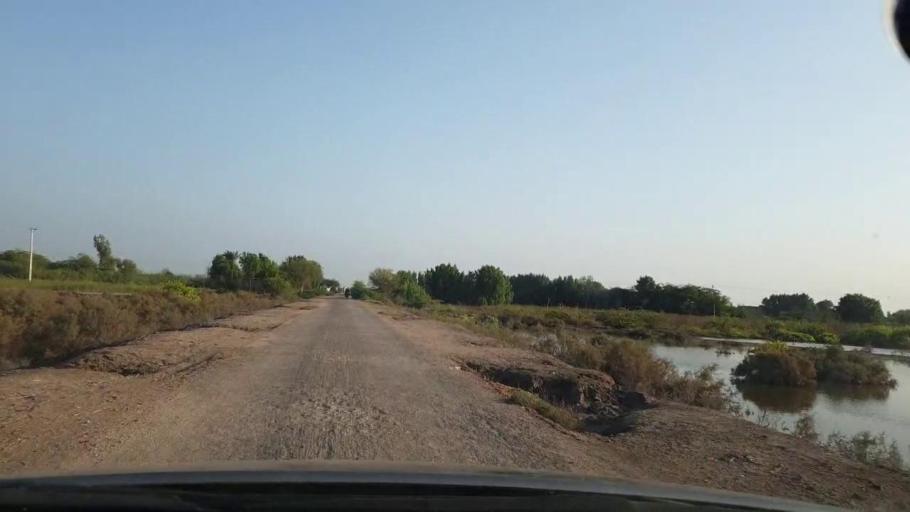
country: PK
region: Sindh
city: Naukot
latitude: 24.7635
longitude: 69.2038
